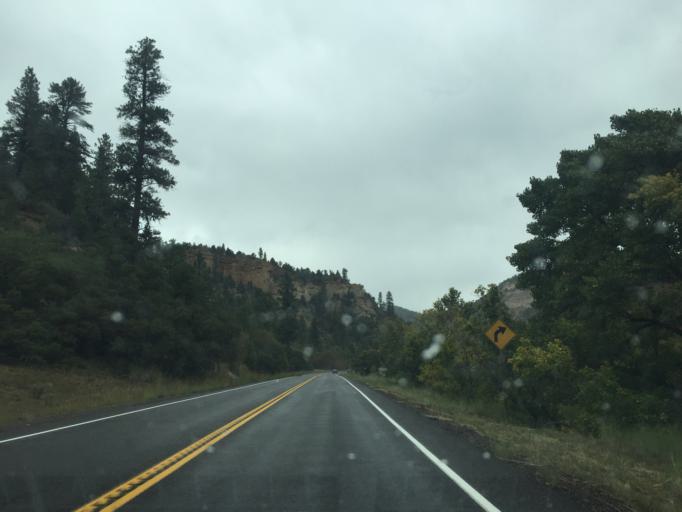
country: US
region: Utah
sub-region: Kane County
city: Kanab
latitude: 37.3705
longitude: -112.5949
